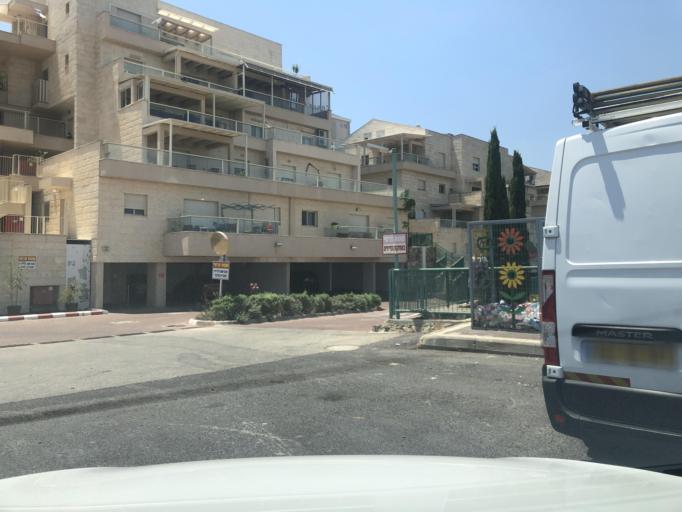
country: IL
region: Haifa
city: Daliyat el Karmil
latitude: 32.6395
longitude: 35.0925
